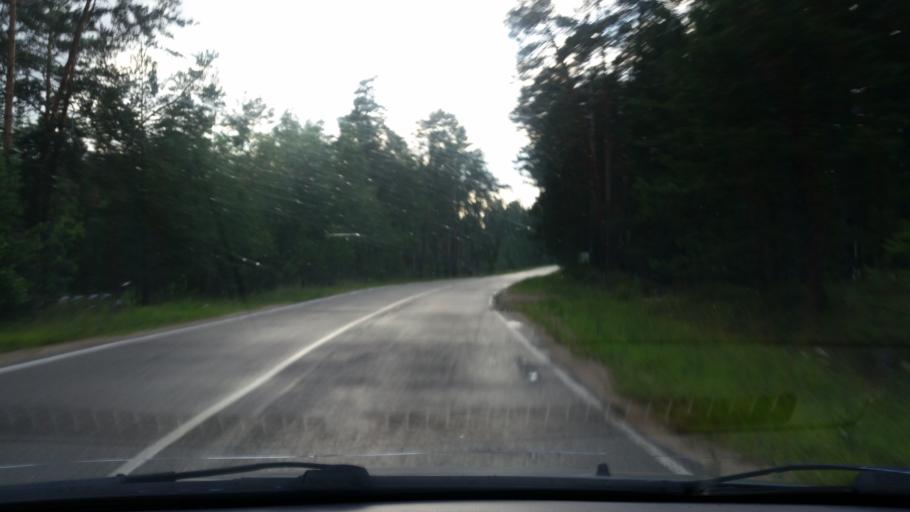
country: RU
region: Moskovskaya
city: Stupino
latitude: 54.8581
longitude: 37.8619
